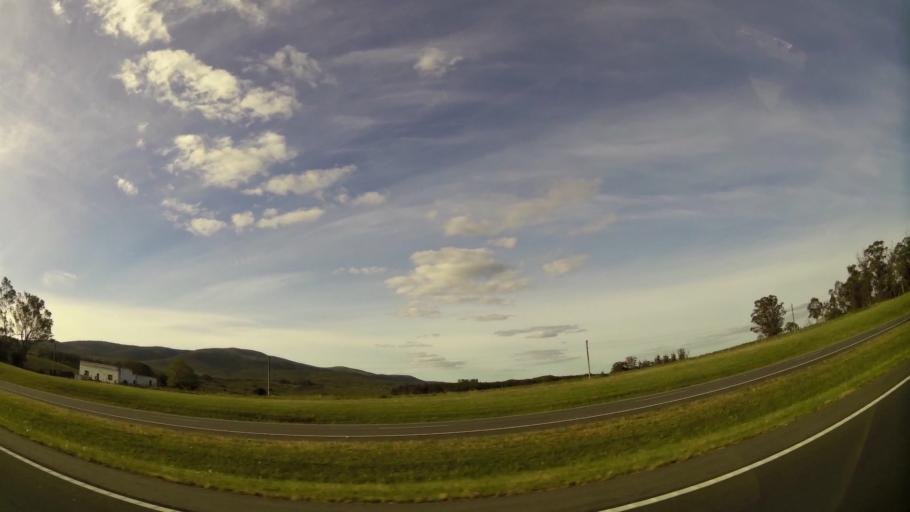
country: UY
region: Maldonado
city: Pan de Azucar
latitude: -34.7882
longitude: -55.2900
